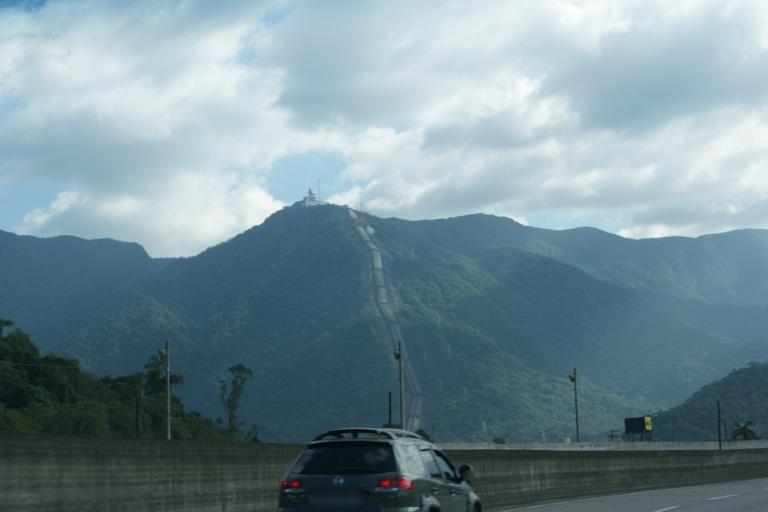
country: BR
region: Sao Paulo
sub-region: Cubatao
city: Cubatao
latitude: -23.8907
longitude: -46.4419
